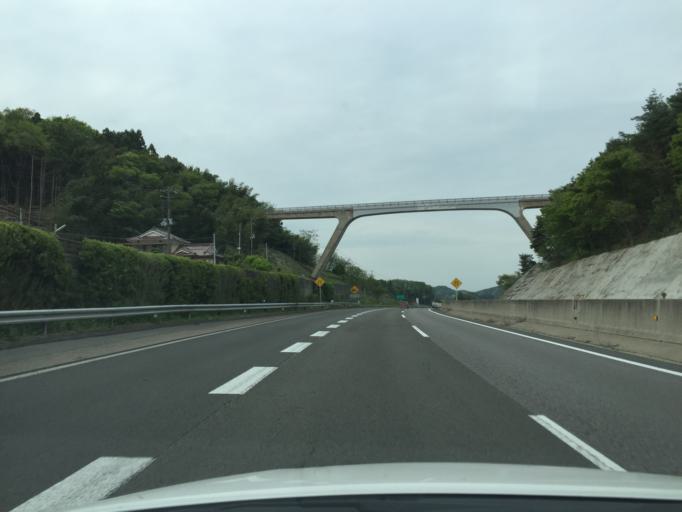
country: JP
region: Fukushima
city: Nihommatsu
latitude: 37.6045
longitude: 140.4216
